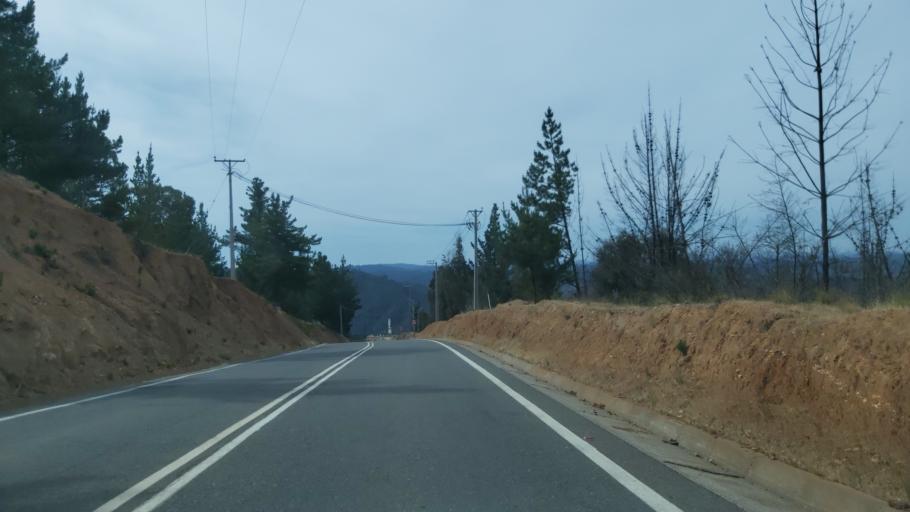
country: CL
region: Maule
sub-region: Provincia de Talca
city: Constitucion
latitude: -34.9136
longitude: -71.9956
